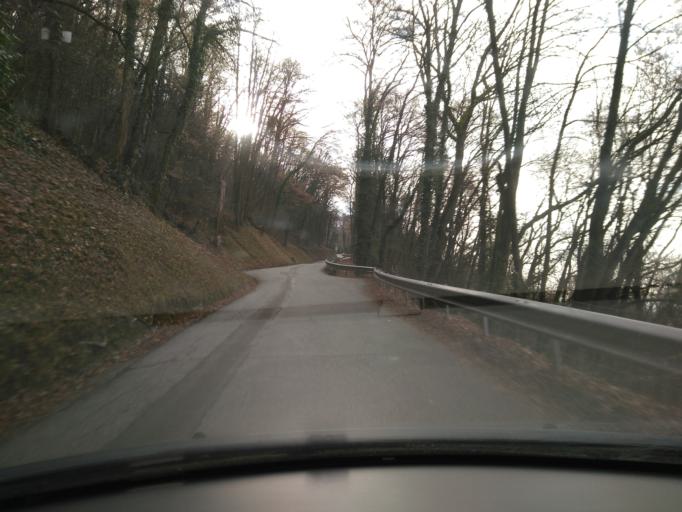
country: FR
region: Rhone-Alpes
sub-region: Departement de l'Isere
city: Villard-Bonnot
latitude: 45.2532
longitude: 5.9078
